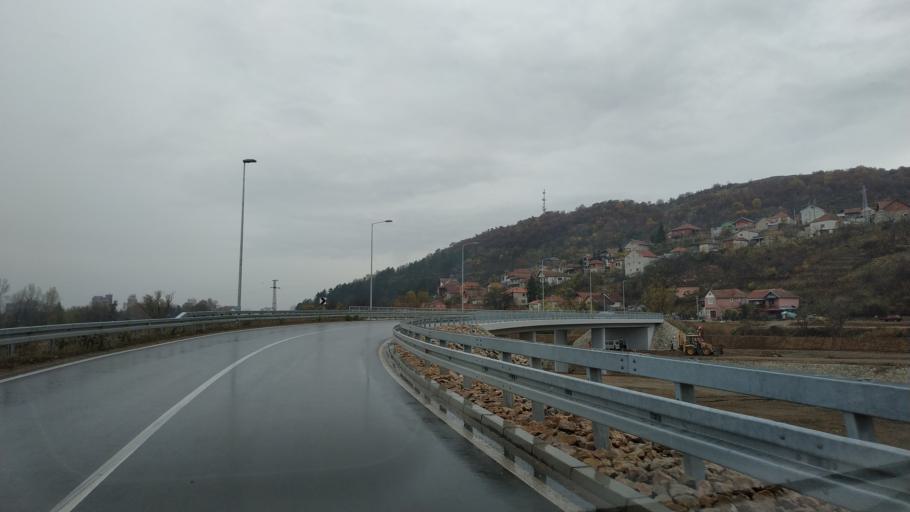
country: RS
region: Central Serbia
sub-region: Pirotski Okrug
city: Pirot
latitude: 43.1659
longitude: 22.5763
